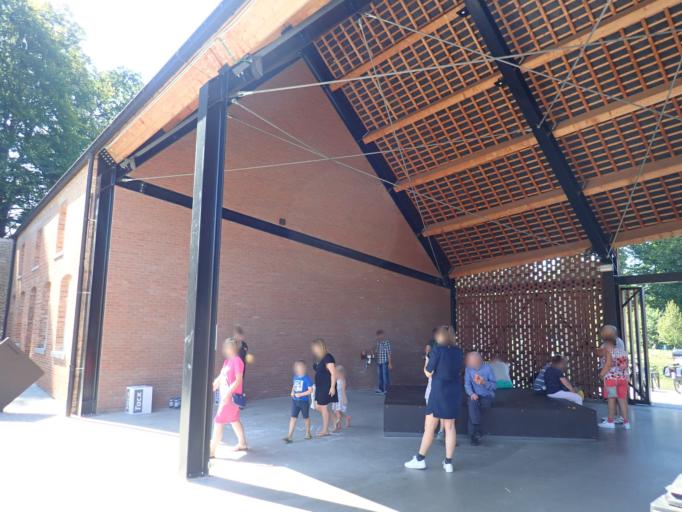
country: BE
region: Flanders
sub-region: Provincie Vlaams-Brabant
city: Scherpenheuvel-Zichem
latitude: 51.0328
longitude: 4.9766
